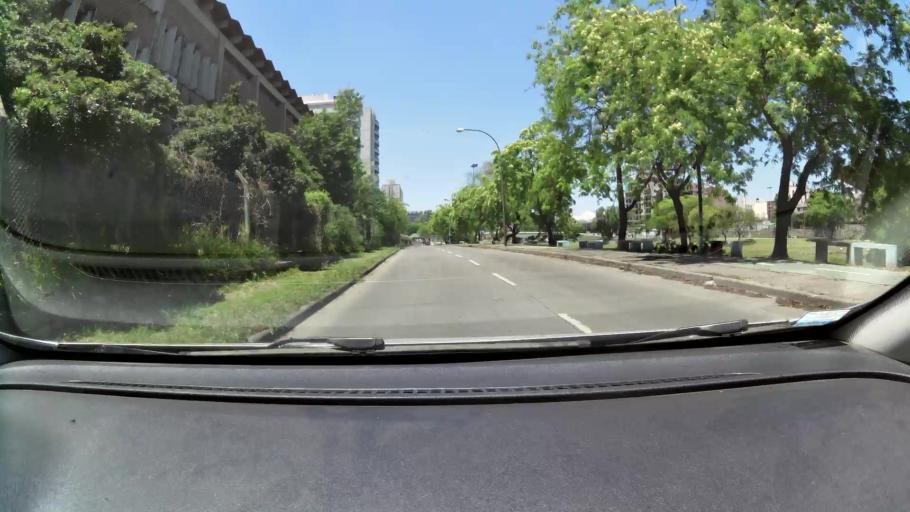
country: AR
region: Cordoba
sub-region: Departamento de Capital
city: Cordoba
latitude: -31.4039
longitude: -64.2015
